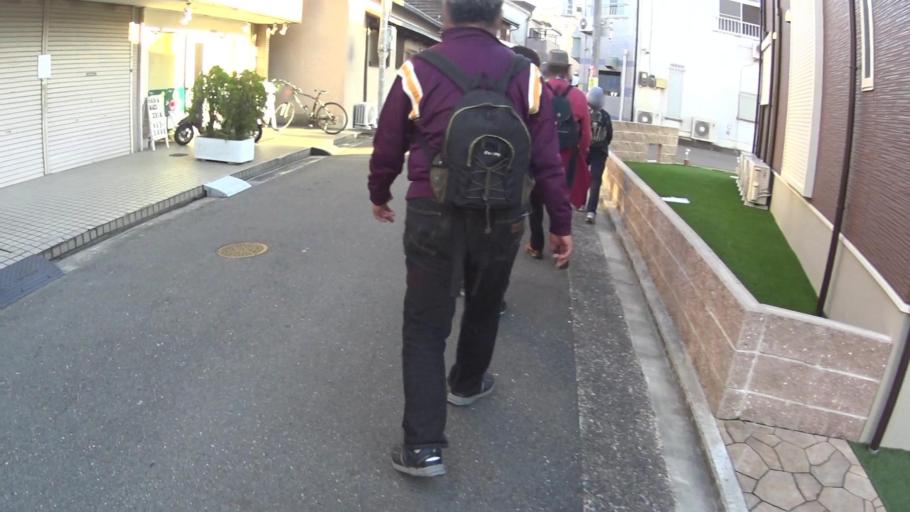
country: JP
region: Osaka
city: Kashihara
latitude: 34.5731
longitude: 135.5955
